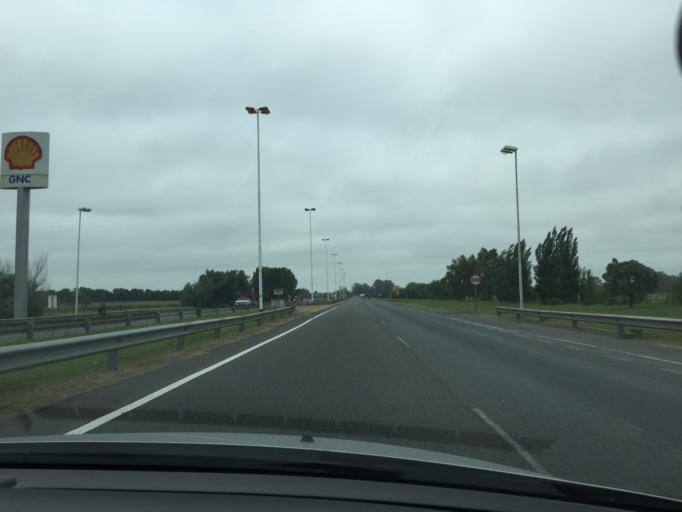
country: AR
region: Buenos Aires
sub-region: Partido de Ezeiza
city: Ezeiza
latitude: -34.8623
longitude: -58.5680
